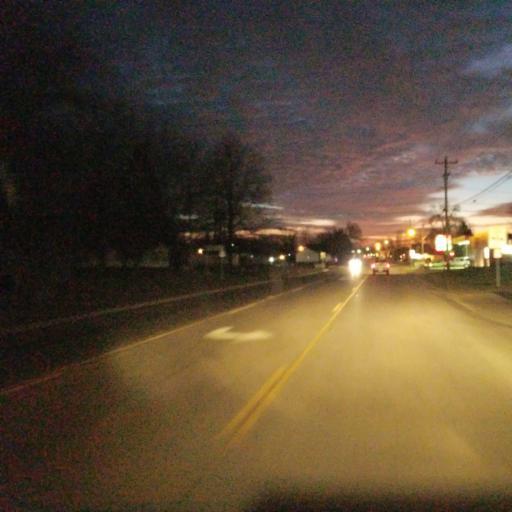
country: US
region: Illinois
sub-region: Peoria County
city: Hanna City
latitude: 40.6928
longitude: -89.8000
